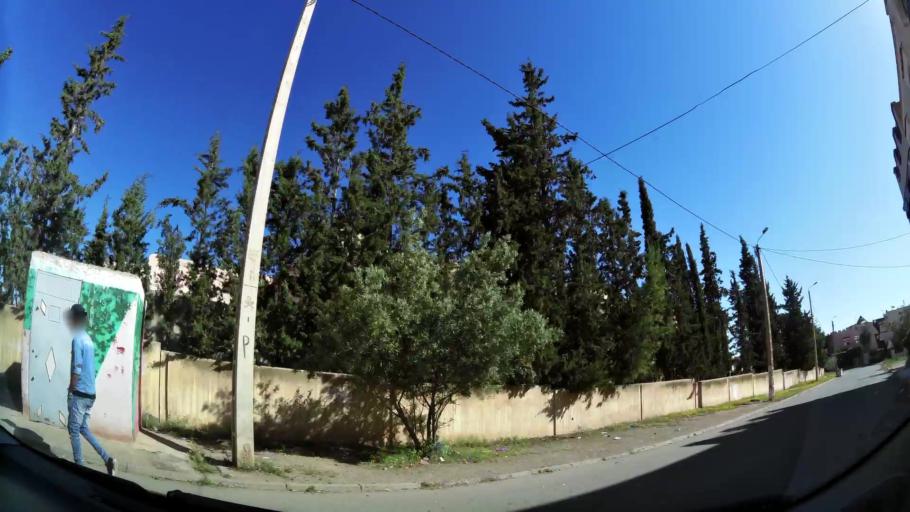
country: MA
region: Oriental
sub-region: Oujda-Angad
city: Oujda
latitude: 34.6555
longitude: -1.8937
